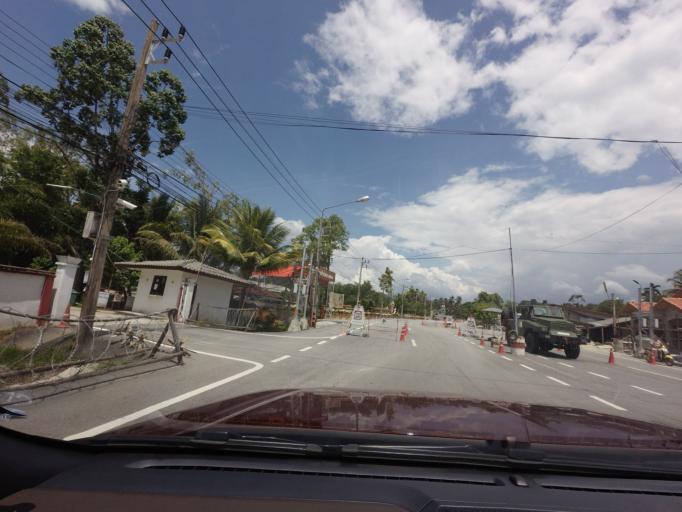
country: TH
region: Narathiwat
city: Chanae
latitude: 6.0990
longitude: 101.6924
